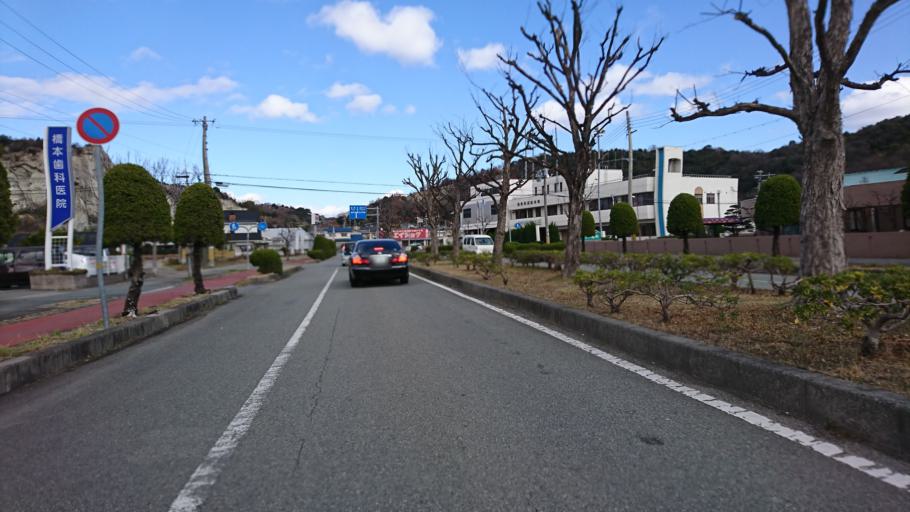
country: JP
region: Hyogo
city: Kakogawacho-honmachi
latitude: 34.7770
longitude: 134.7902
